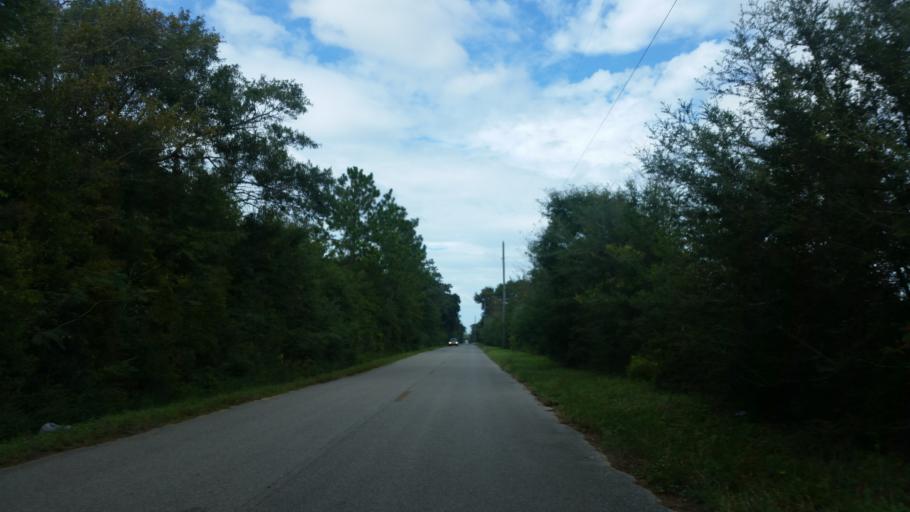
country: US
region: Florida
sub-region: Santa Rosa County
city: Point Baker
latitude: 30.7154
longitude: -86.9929
